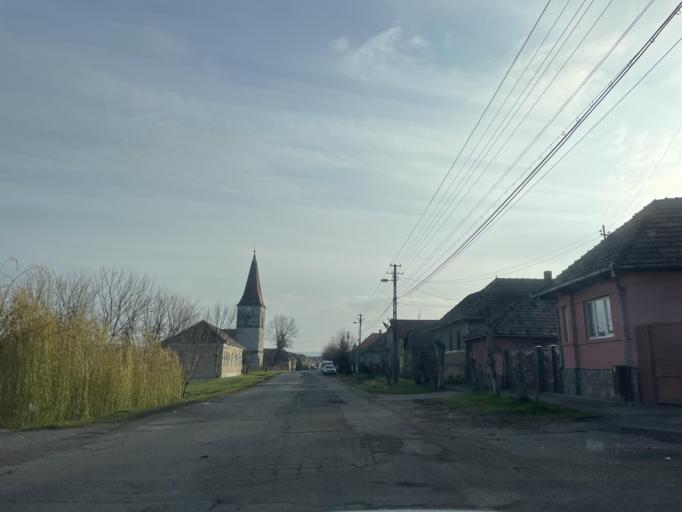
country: RO
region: Mures
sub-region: Municipiul Reghin
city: Apalina
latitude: 46.7508
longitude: 24.6934
